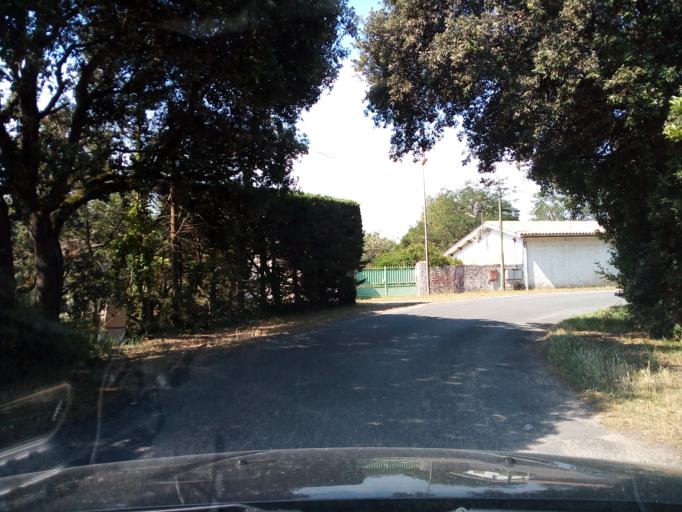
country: FR
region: Poitou-Charentes
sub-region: Departement de la Charente-Maritime
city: Boyard-Ville
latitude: 45.9569
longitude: -1.2581
